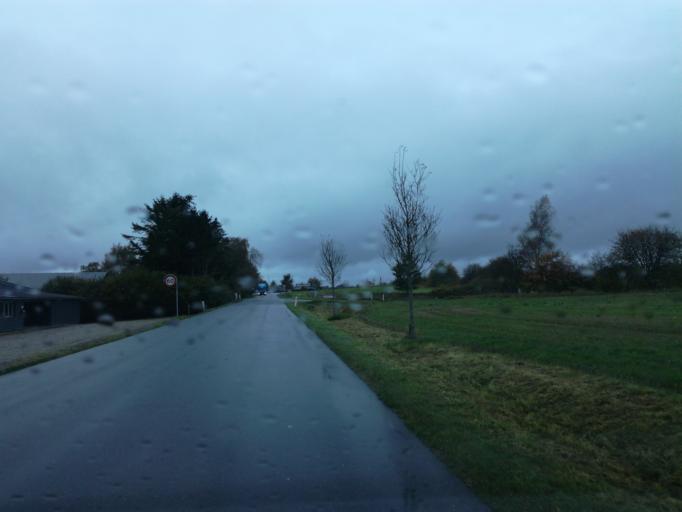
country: DK
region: South Denmark
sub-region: Vejle Kommune
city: Borkop
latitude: 55.6449
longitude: 9.6612
